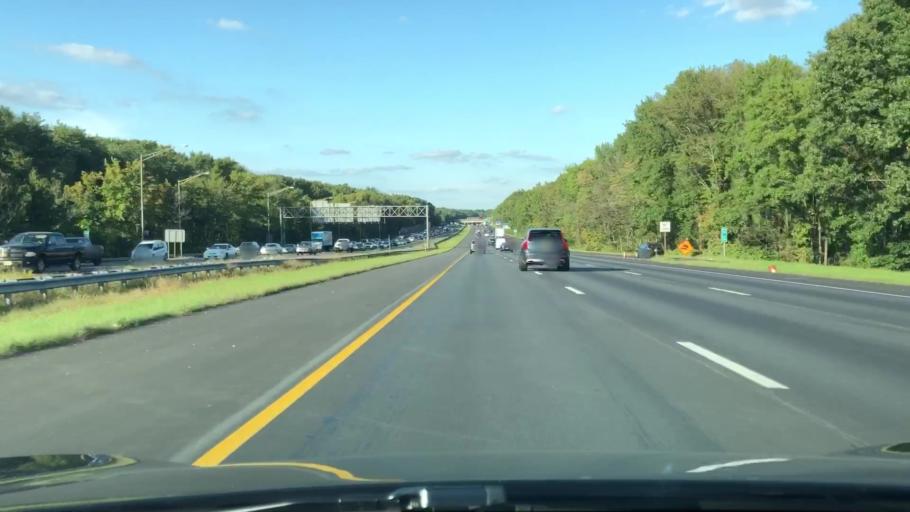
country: US
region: New Jersey
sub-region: Camden County
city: Kingston Estates
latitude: 39.9112
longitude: -74.9831
